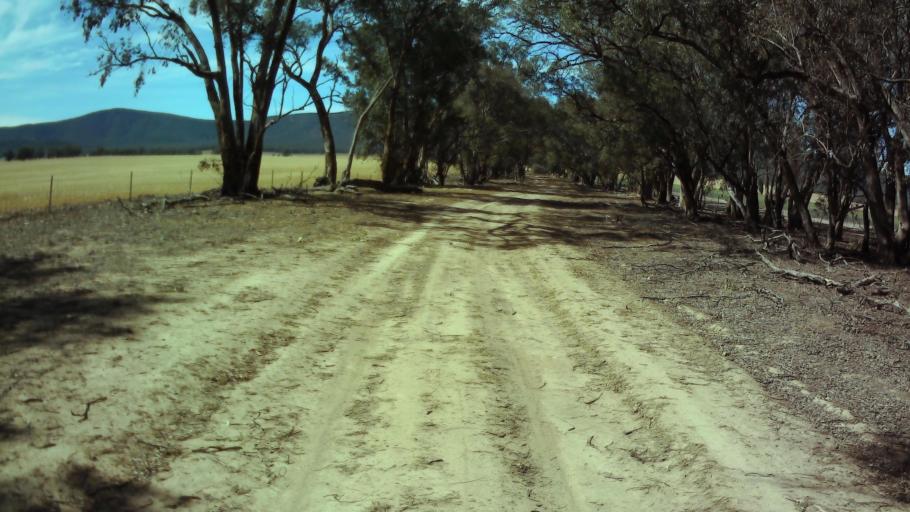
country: AU
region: New South Wales
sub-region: Weddin
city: Grenfell
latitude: -33.9394
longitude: 148.0479
